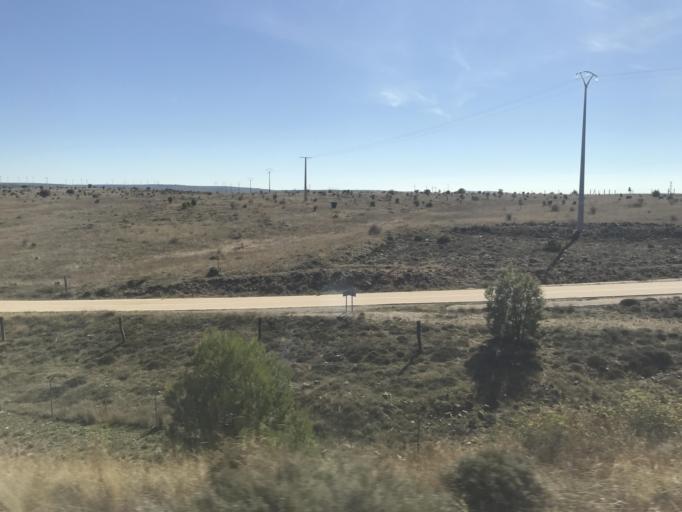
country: ES
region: Castille-La Mancha
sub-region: Provincia de Guadalajara
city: Anguita
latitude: 41.1169
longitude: -2.3543
